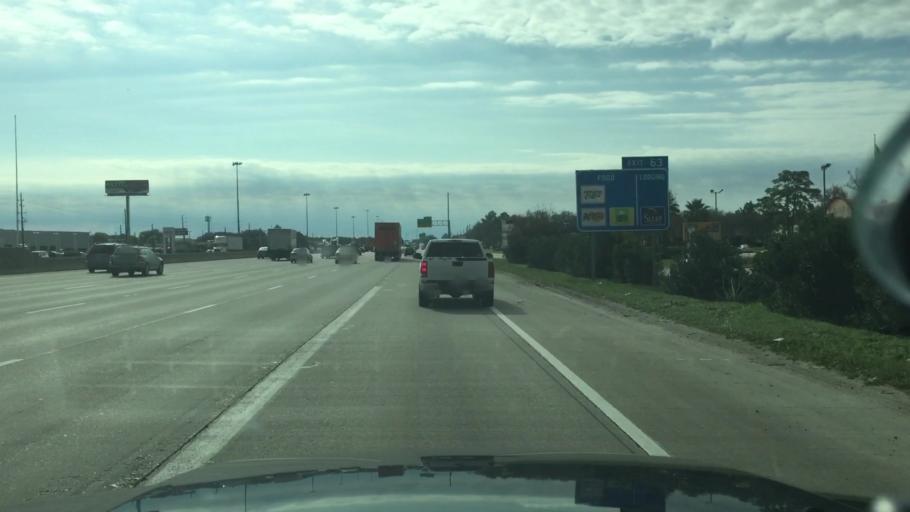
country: US
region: Texas
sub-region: Harris County
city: Aldine
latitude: 29.9922
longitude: -95.4248
